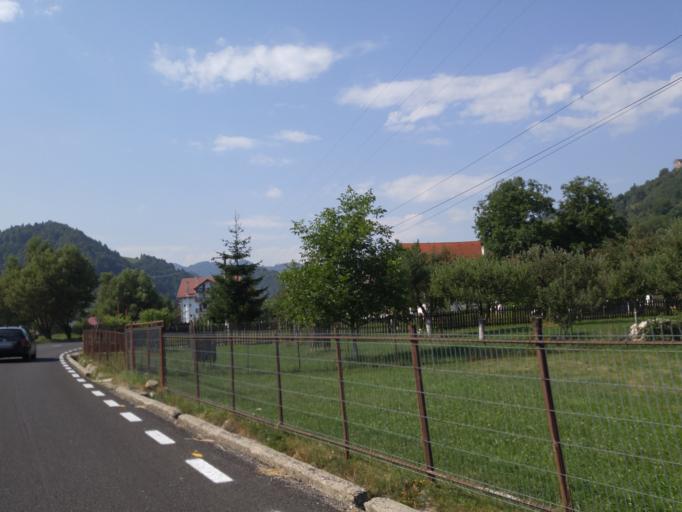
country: RO
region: Brasov
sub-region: Municipiul Brasov
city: Moeciu de Jos
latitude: 45.4893
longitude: 25.3251
